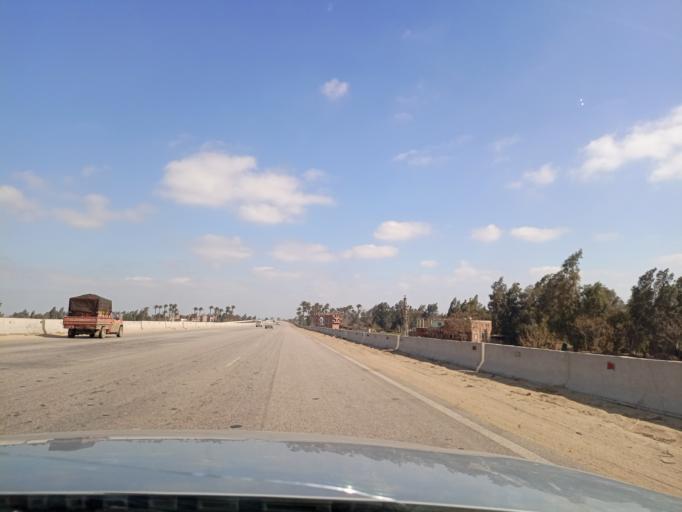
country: EG
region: Muhafazat al Qalyubiyah
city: Banha
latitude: 30.4432
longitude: 31.1166
